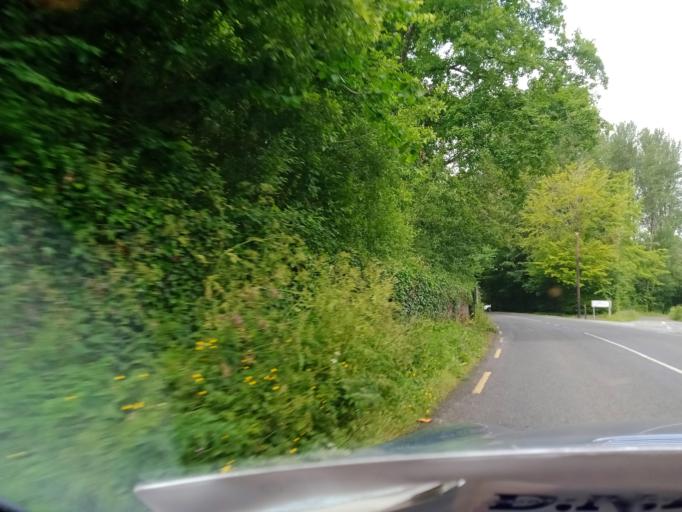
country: IE
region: Leinster
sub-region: Kilkenny
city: Piltown
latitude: 52.4704
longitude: -7.2767
